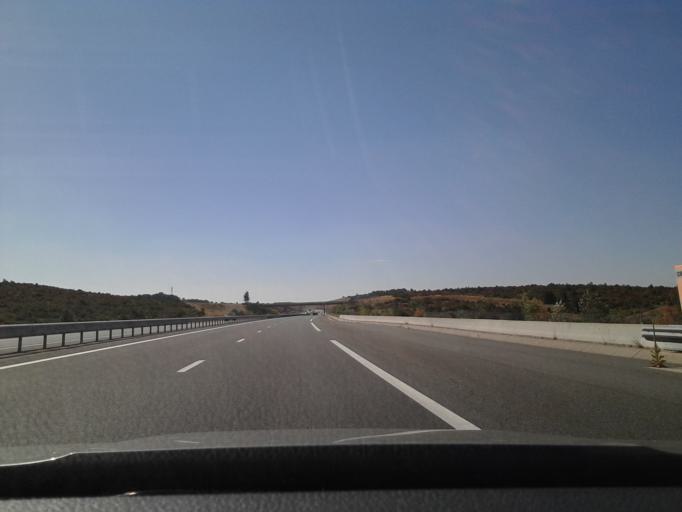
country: FR
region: Midi-Pyrenees
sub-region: Departement de l'Aveyron
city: Creissels
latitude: 44.0469
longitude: 3.0532
